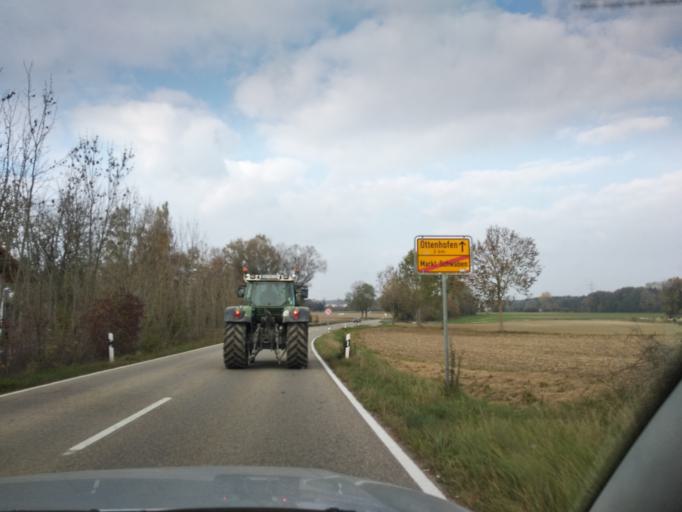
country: DE
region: Bavaria
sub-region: Upper Bavaria
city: Markt Schwaben
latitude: 48.1977
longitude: 11.8757
